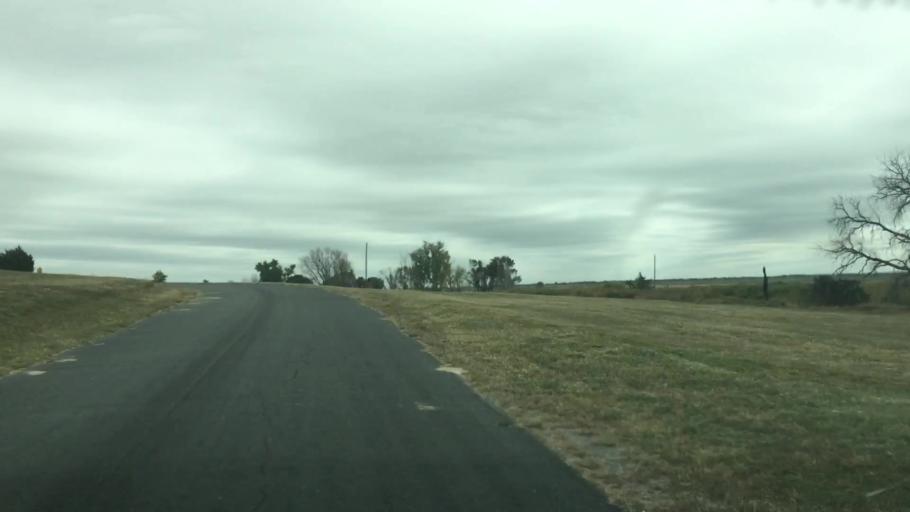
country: US
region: Kansas
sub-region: Hamilton County
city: Syracuse
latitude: 38.0576
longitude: -102.1112
